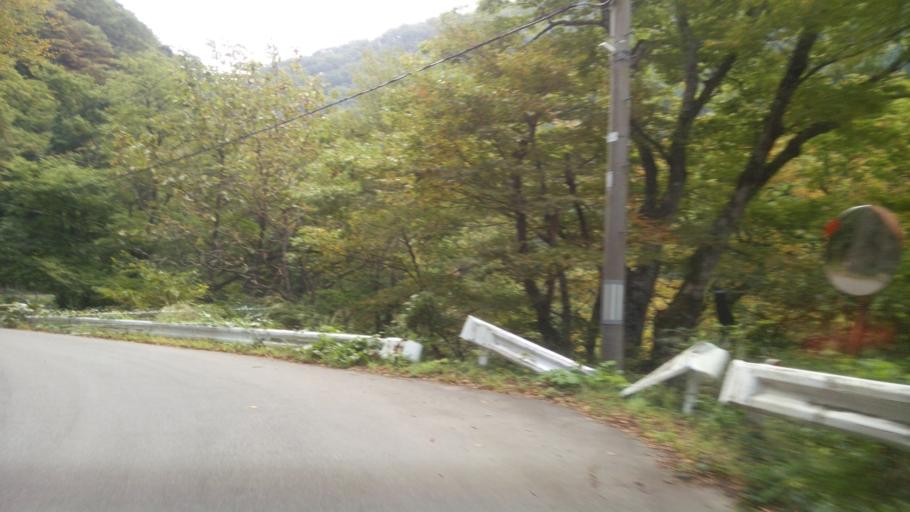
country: JP
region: Fukushima
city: Inawashiro
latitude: 37.3815
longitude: 139.9393
